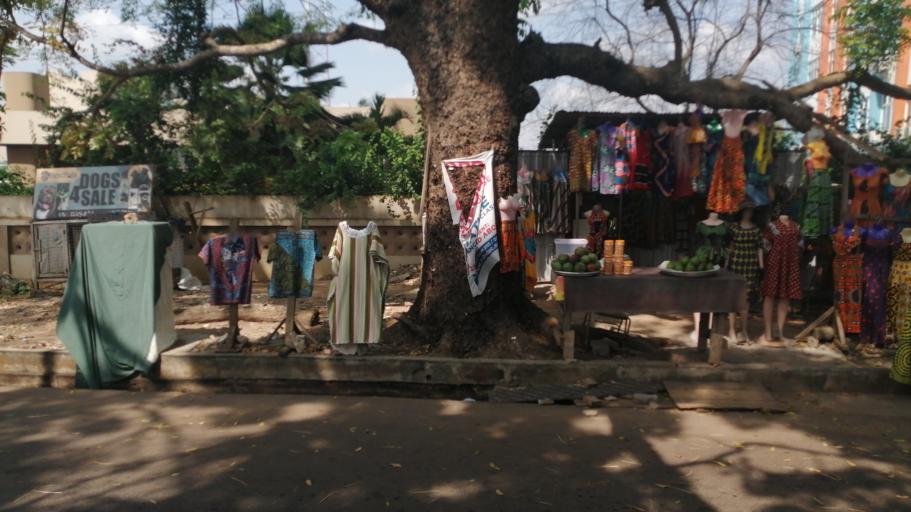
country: GH
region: Greater Accra
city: Medina Estates
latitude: 5.6376
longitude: -0.1715
